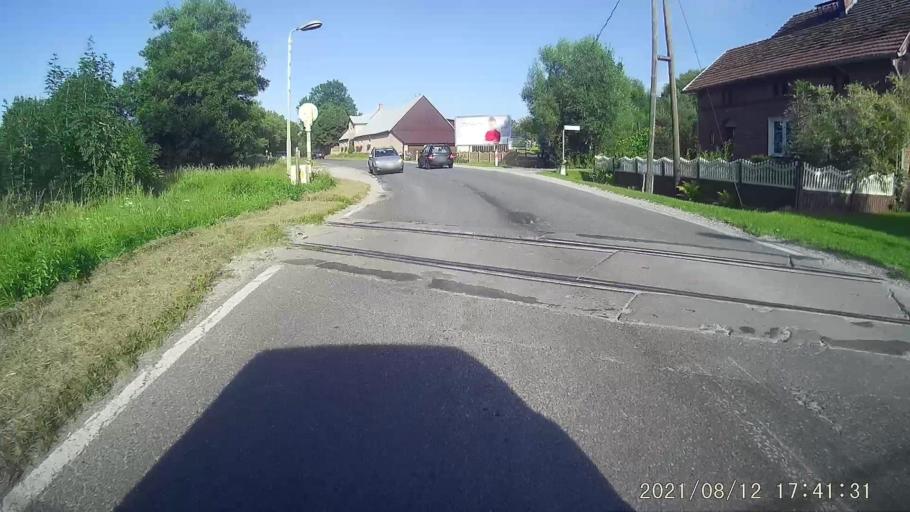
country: PL
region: Lower Silesian Voivodeship
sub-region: Powiat klodzki
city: Ladek-Zdroj
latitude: 50.3397
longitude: 16.8252
